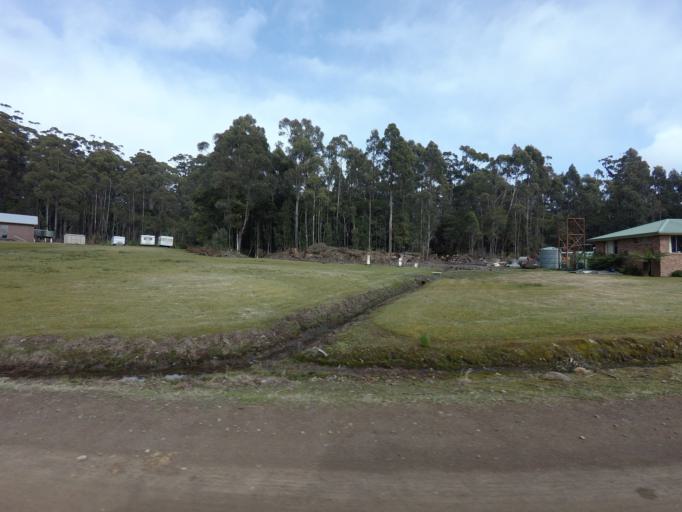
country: AU
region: Tasmania
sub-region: Huon Valley
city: Geeveston
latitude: -43.5391
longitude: 146.8919
